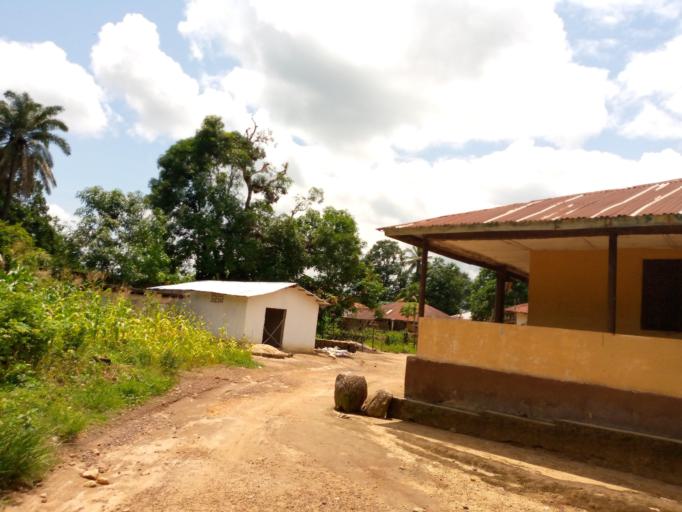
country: SL
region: Northern Province
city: Magburaka
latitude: 8.7303
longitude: -11.9443
